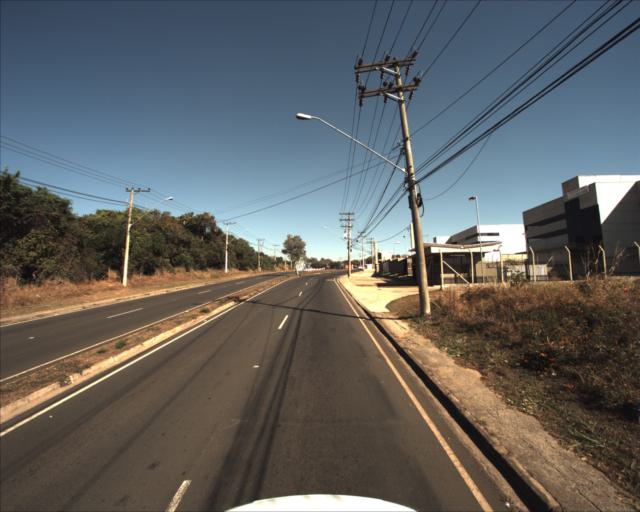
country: BR
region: Sao Paulo
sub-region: Sorocaba
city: Sorocaba
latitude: -23.4527
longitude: -47.4183
